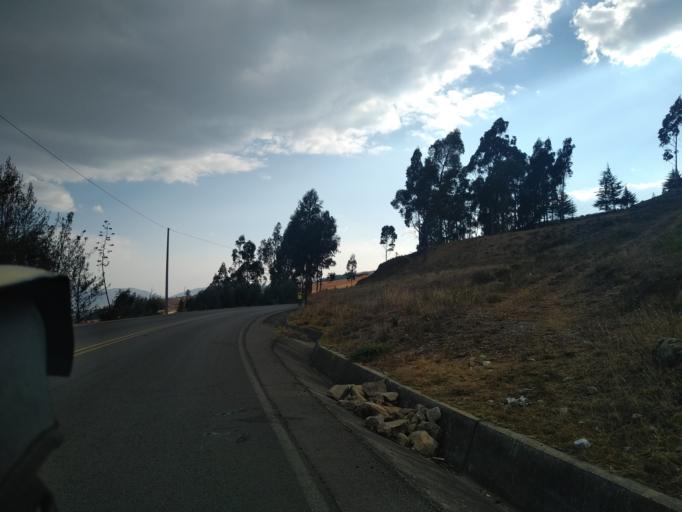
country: PE
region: Cajamarca
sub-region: Provincia de Cajamarca
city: Llacanora
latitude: -7.1518
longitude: -78.4128
